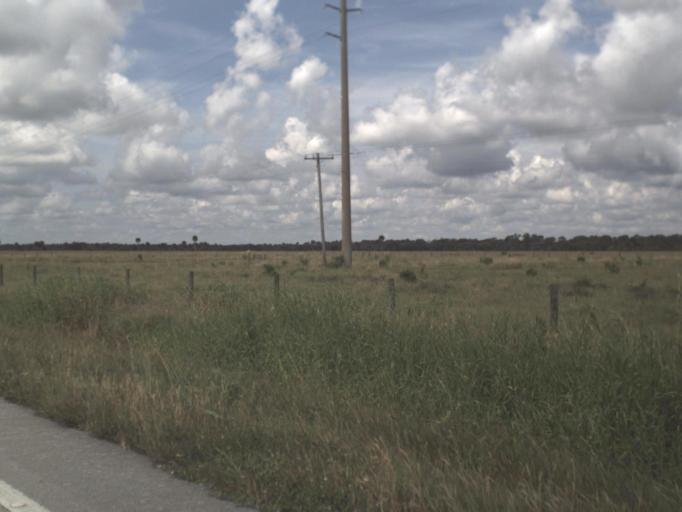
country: US
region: Florida
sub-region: Okeechobee County
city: Okeechobee
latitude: 27.2436
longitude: -80.9430
